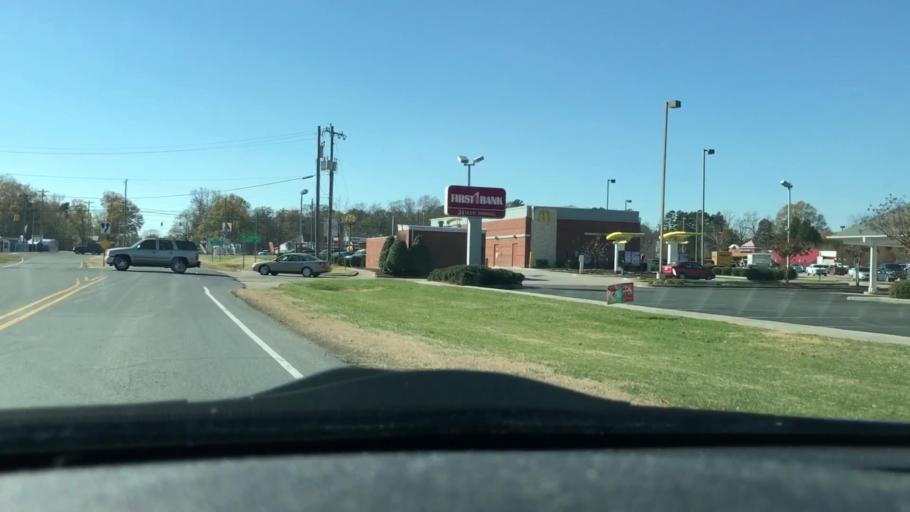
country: US
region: North Carolina
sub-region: Stanly County
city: Albemarle
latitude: 35.4723
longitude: -80.2659
